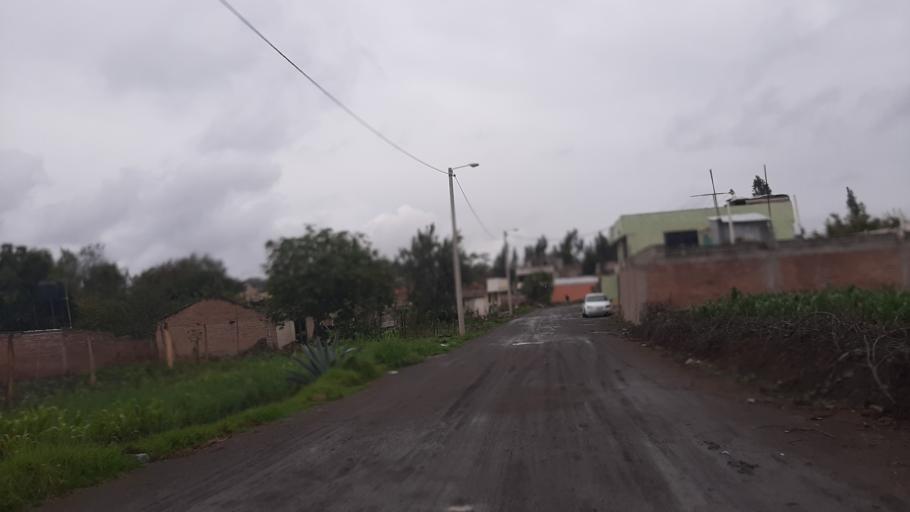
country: EC
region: Chimborazo
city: Riobamba
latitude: -1.6551
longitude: -78.6373
